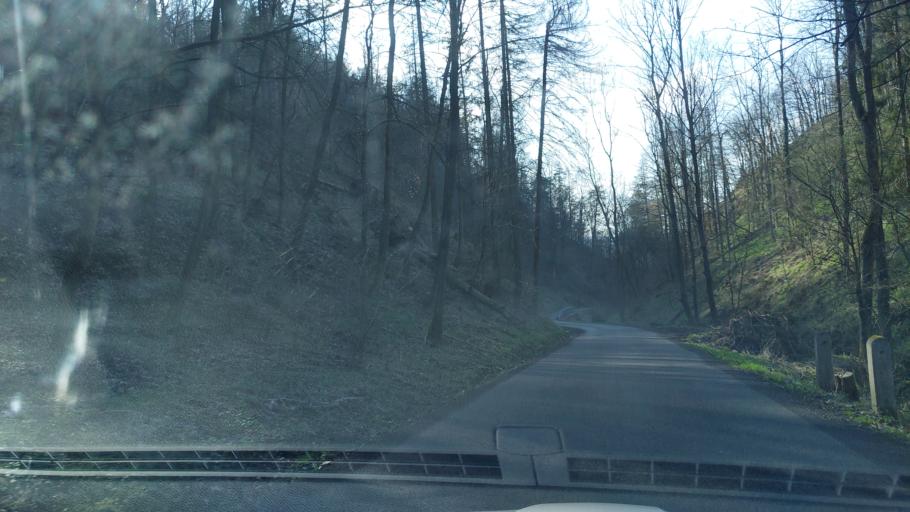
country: CZ
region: Ustecky
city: Vernerice
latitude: 50.7019
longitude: 14.2345
